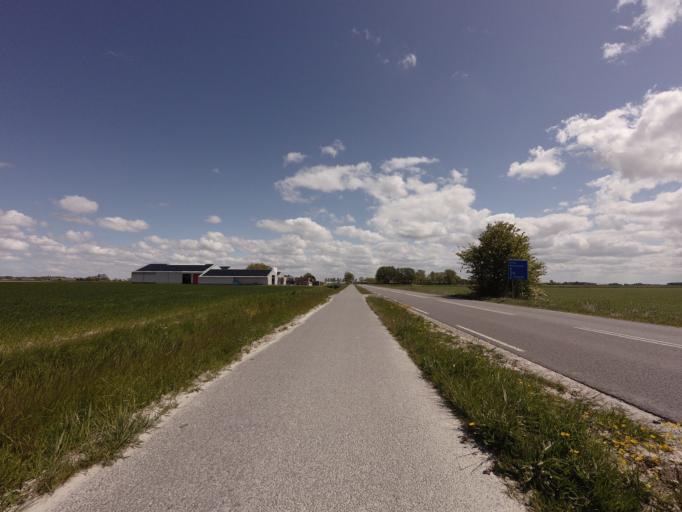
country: NL
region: Friesland
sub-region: Gemeente Harlingen
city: Harlingen
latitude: 53.1367
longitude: 5.4584
